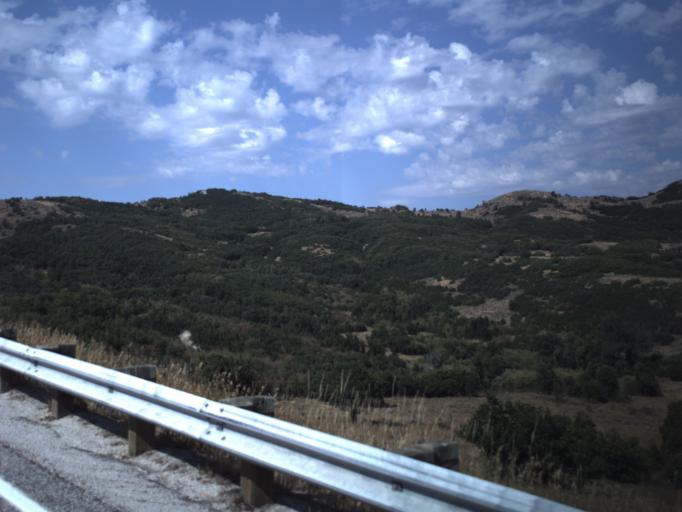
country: US
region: Utah
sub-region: Morgan County
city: Mountain Green
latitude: 41.1689
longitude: -111.8028
